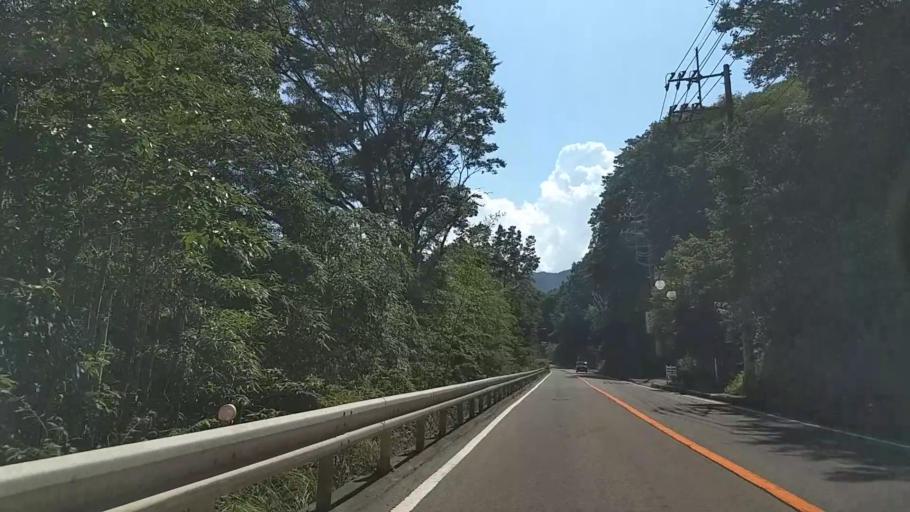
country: JP
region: Yamanashi
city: Ryuo
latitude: 35.4796
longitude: 138.4465
